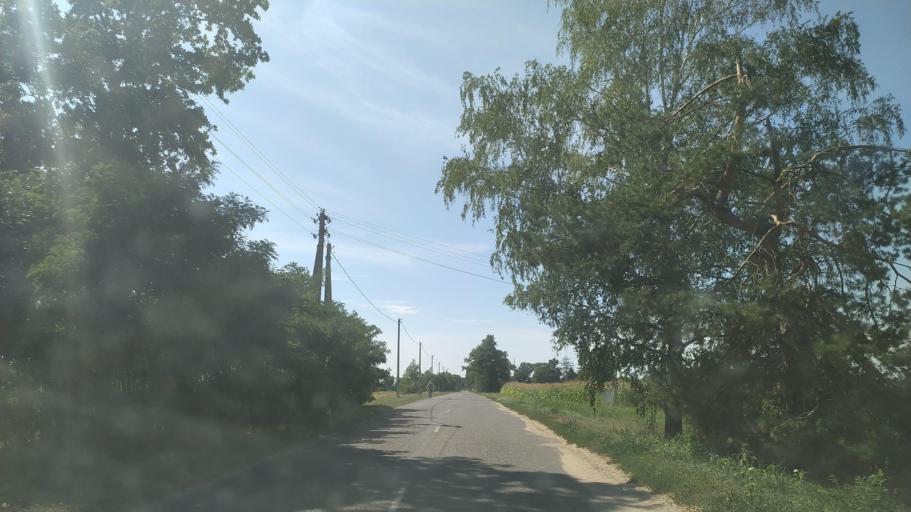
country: BY
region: Brest
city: Byaroza
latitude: 52.3891
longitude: 25.0313
